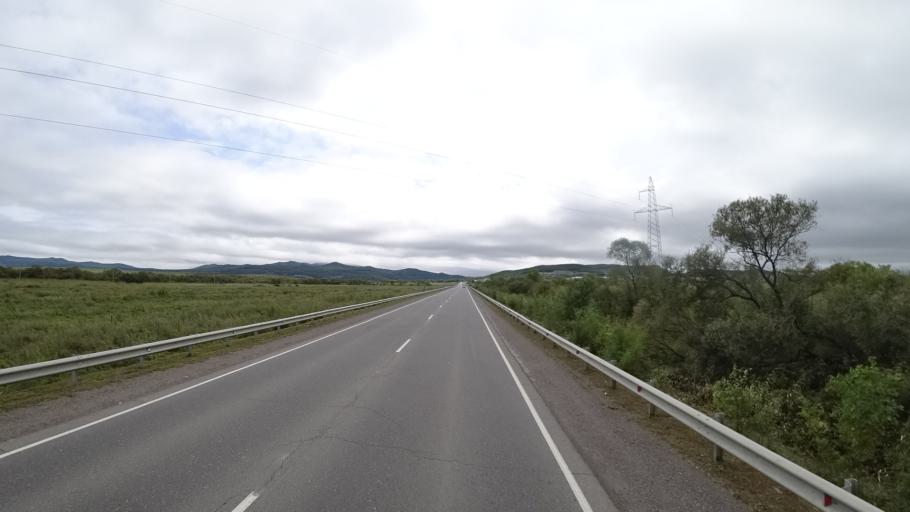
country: RU
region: Primorskiy
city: Monastyrishche
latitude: 44.1805
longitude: 132.4415
